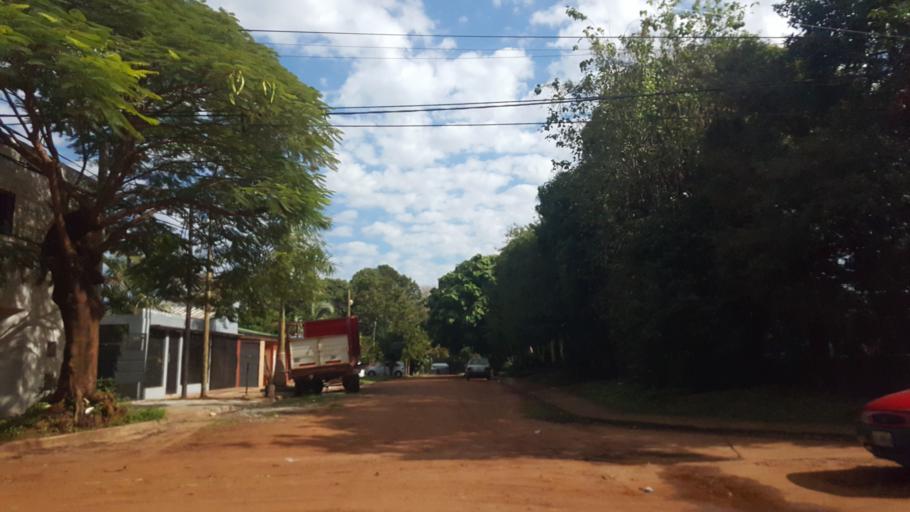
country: AR
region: Misiones
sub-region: Departamento de Capital
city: Posadas
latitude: -27.3708
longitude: -55.9226
